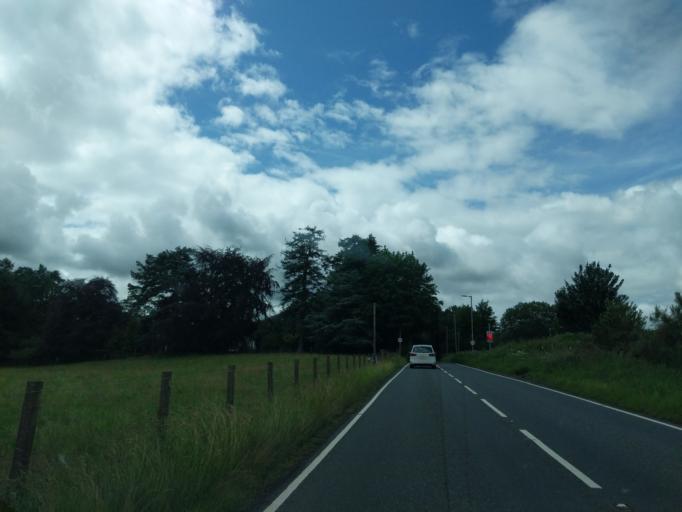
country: GB
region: Scotland
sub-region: South Lanarkshire
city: Biggar
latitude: 55.6049
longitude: -3.5918
